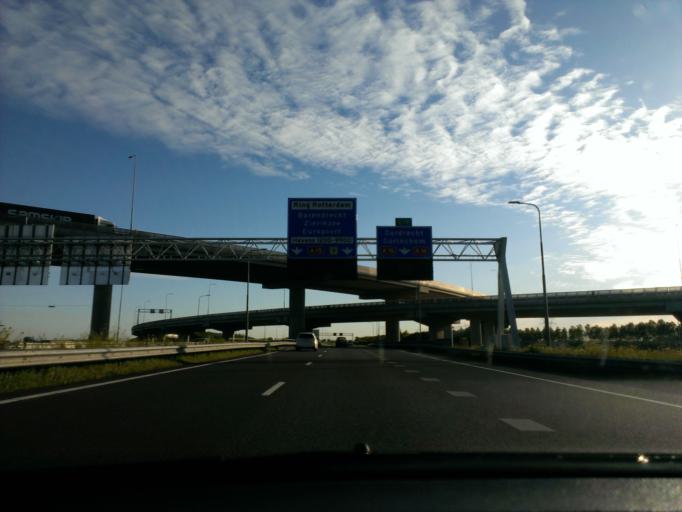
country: NL
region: South Holland
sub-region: Gemeente Ridderkerk
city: Ridderkerk
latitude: 51.8753
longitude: 4.5724
